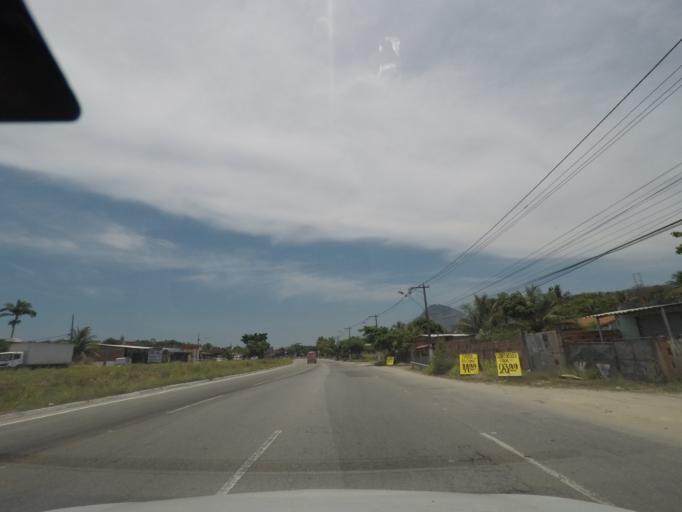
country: BR
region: Rio de Janeiro
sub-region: Marica
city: Marica
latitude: -22.9305
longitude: -42.8747
